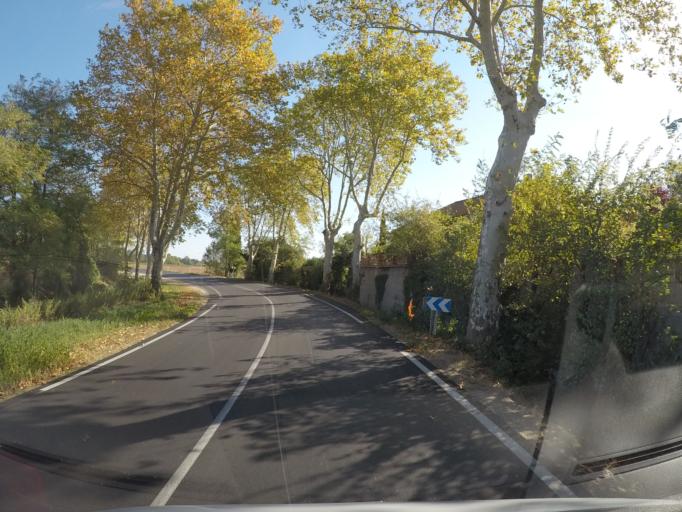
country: FR
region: Languedoc-Roussillon
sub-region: Departement du Gard
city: Lezan
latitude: 44.0197
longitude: 4.0548
